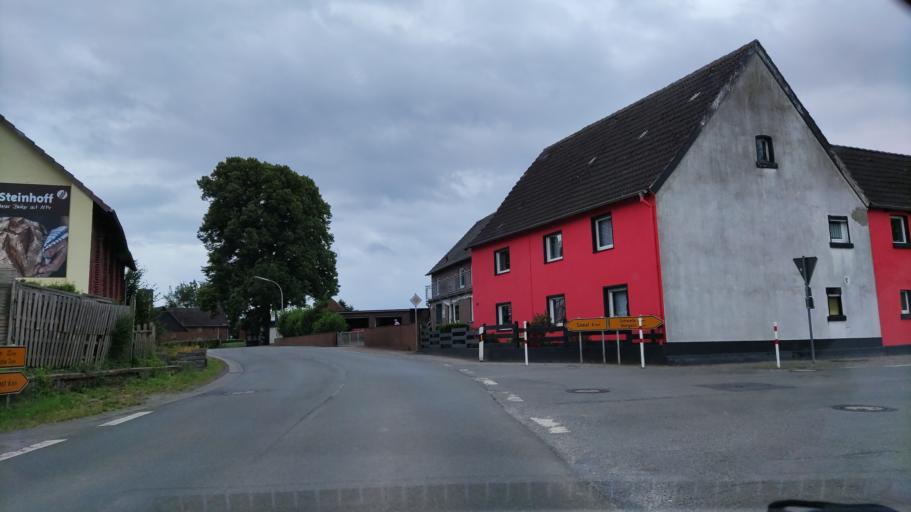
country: DE
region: North Rhine-Westphalia
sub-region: Regierungsbezirk Arnsberg
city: Soest
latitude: 51.6047
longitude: 8.0466
